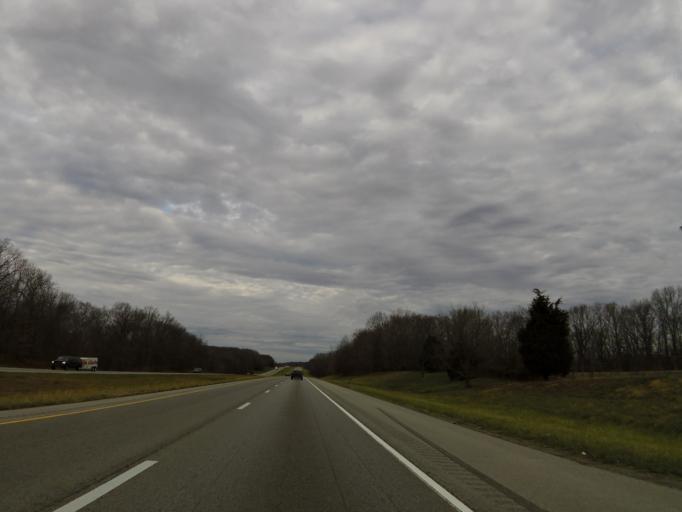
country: US
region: Illinois
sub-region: Clinton County
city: Wamac
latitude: 38.3674
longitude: -89.0897
